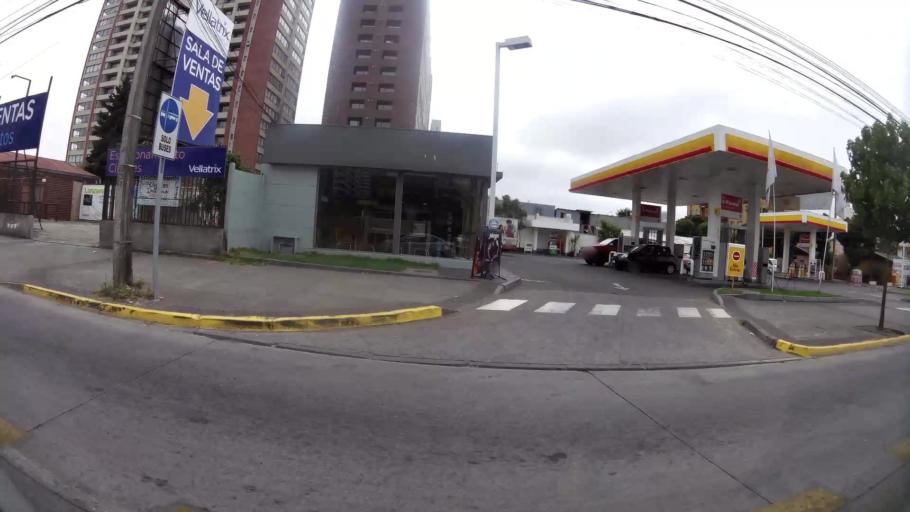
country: CL
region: Biobio
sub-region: Provincia de Concepcion
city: Concepcion
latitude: -36.8192
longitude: -73.0424
